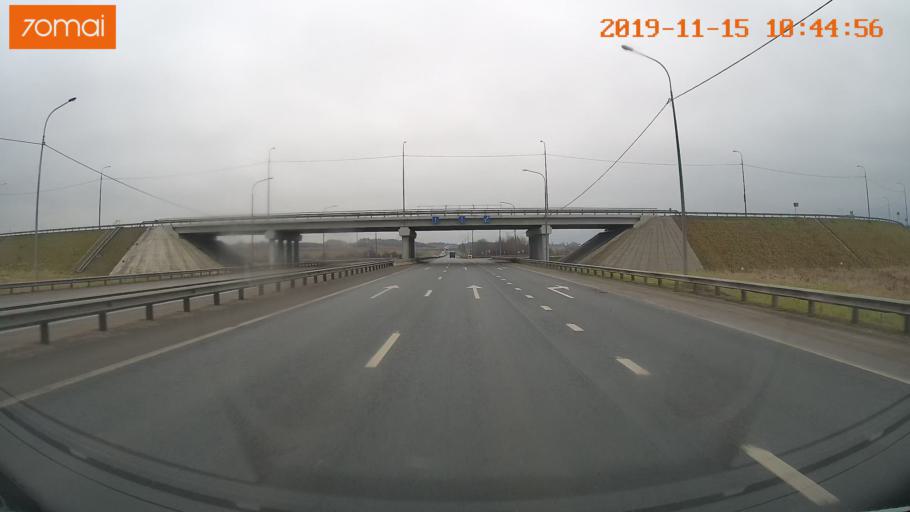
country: RU
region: Vologda
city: Sheksna
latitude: 59.2113
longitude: 38.5725
